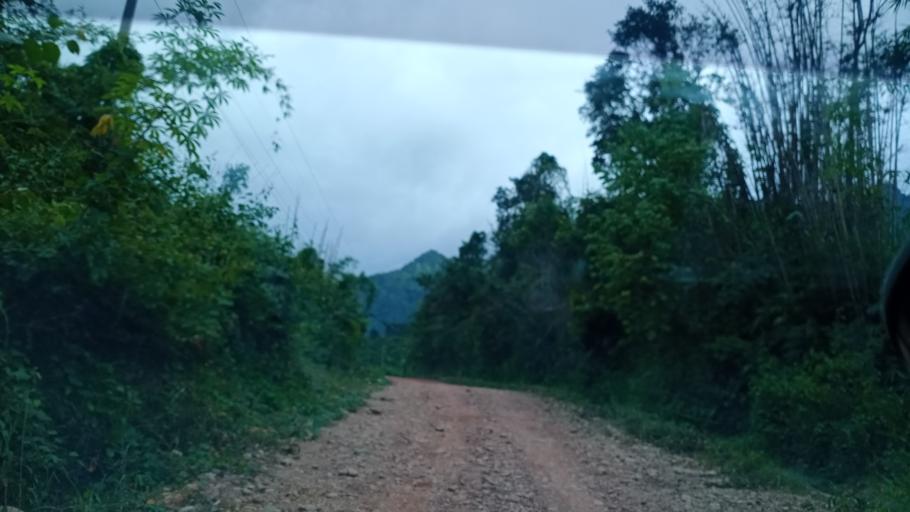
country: TH
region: Changwat Bueng Kan
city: Pak Khat
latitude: 18.7222
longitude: 103.2483
